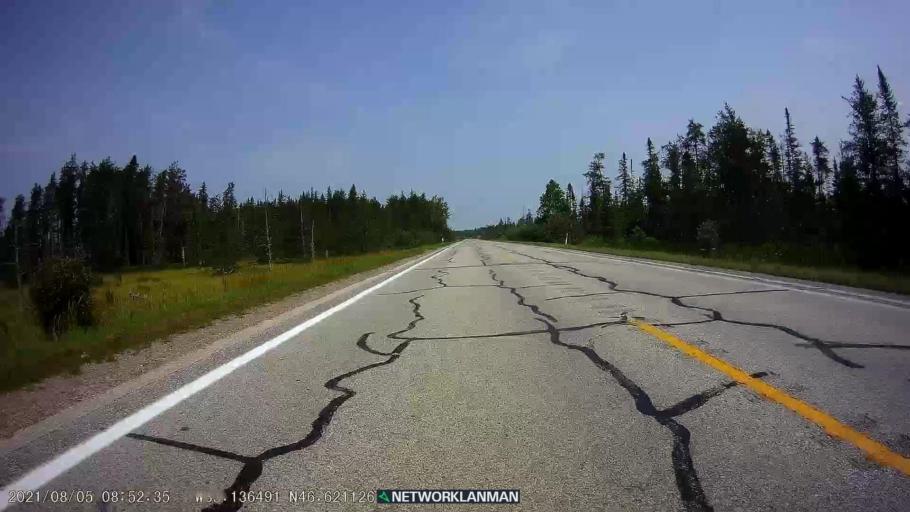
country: US
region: Michigan
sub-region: Luce County
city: Newberry
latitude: 46.6208
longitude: -85.1365
